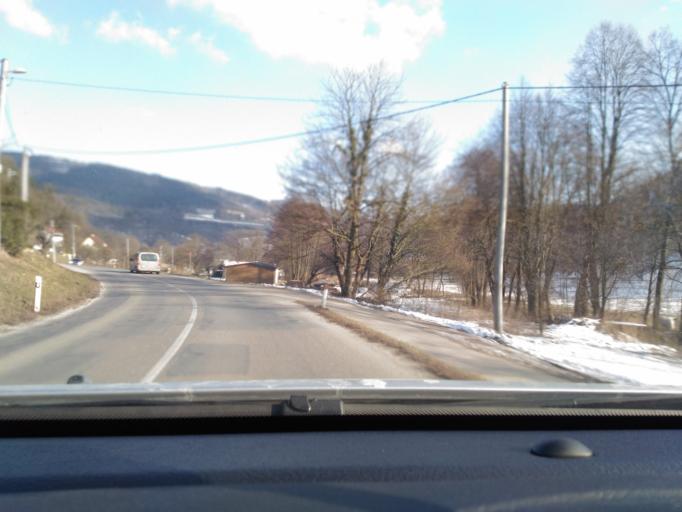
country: CZ
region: South Moravian
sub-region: Okres Brno-Venkov
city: Dolni Loucky
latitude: 49.4019
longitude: 16.3547
